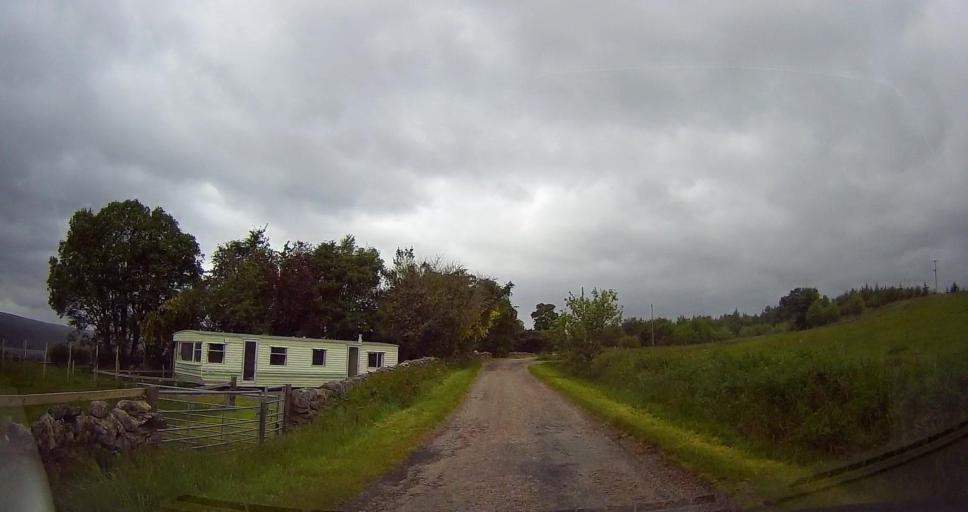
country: GB
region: Scotland
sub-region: Highland
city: Alness
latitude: 58.0801
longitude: -4.4479
